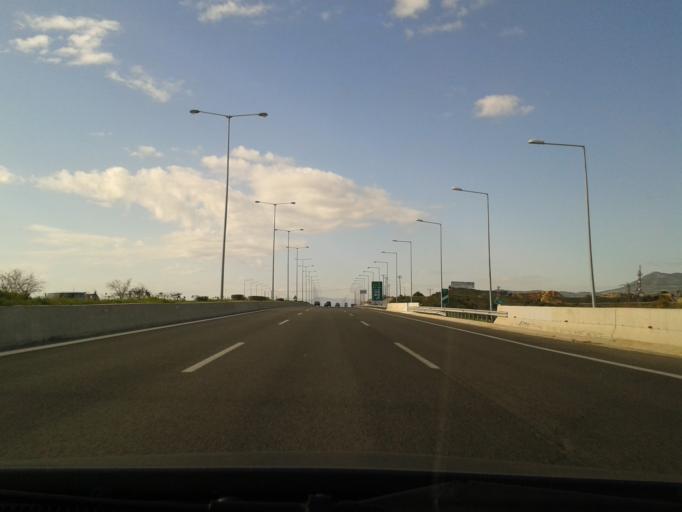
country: GR
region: Attica
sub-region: Nomarchia Dytikis Attikis
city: Megara
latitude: 37.9991
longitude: 23.3721
